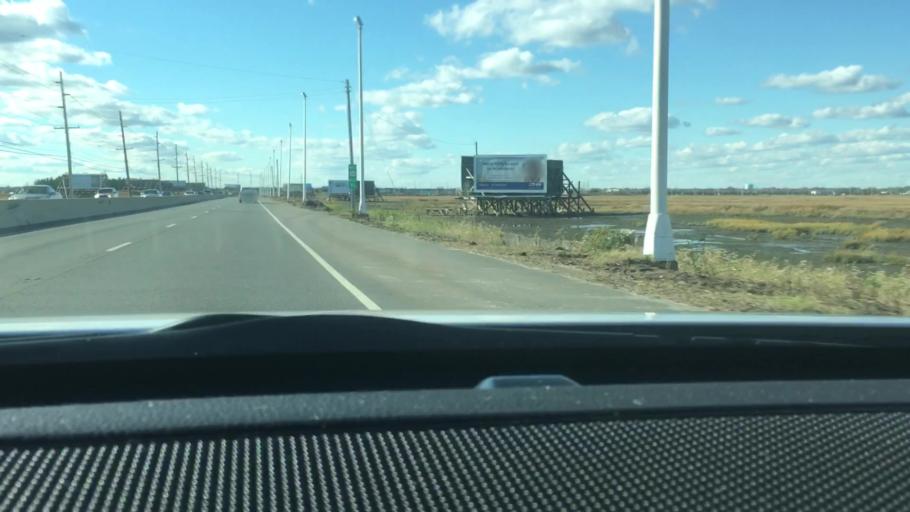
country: US
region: New Jersey
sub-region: Atlantic County
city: Absecon
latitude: 39.3885
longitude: -74.4800
